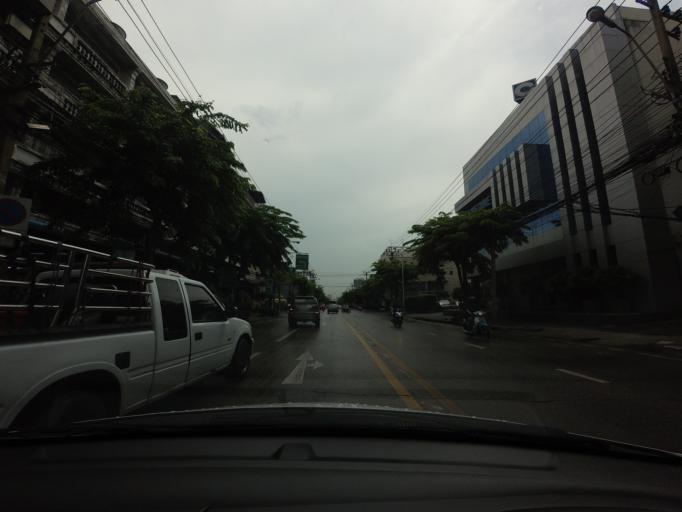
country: TH
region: Bangkok
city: Phra Khanong
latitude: 13.7101
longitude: 100.6298
